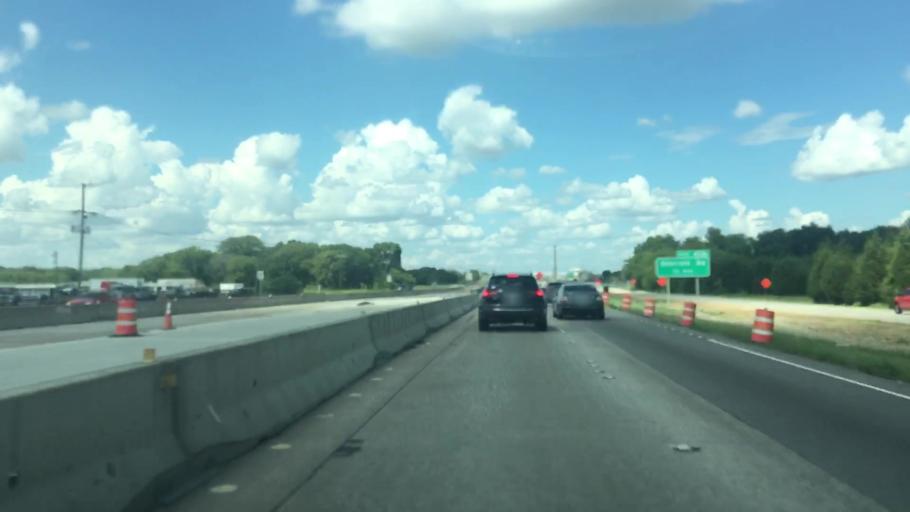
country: US
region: Texas
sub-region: Ellis County
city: Oak Leaf
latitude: 32.4656
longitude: -96.8412
